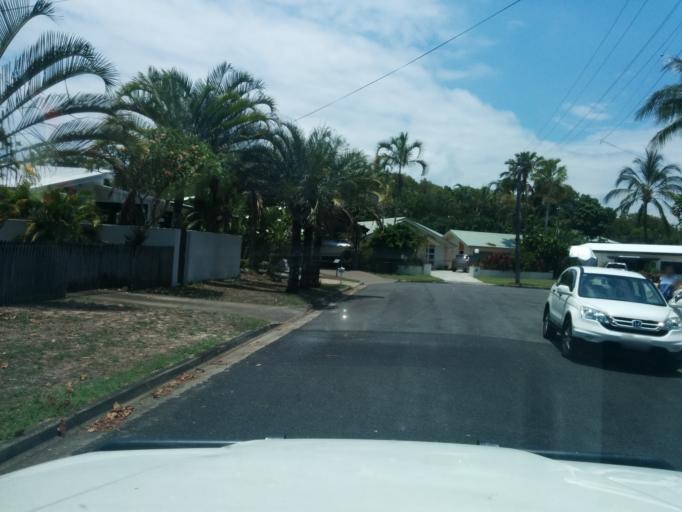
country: AU
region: Queensland
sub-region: Cairns
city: Yorkeys Knob
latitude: -16.8382
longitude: 145.7388
